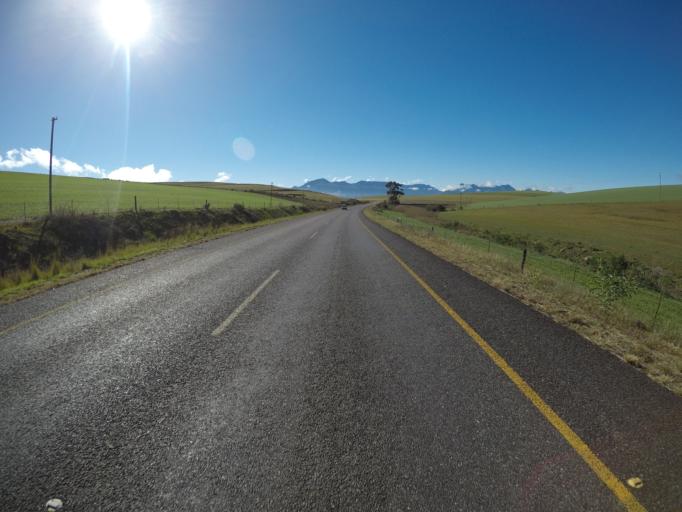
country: ZA
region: Western Cape
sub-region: Overberg District Municipality
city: Caledon
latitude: -34.1356
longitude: 19.5088
